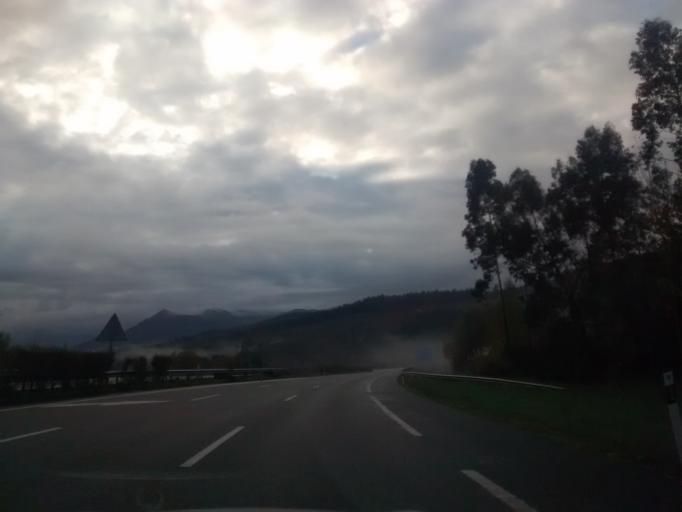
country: ES
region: Cantabria
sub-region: Provincia de Cantabria
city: Barcena de Cicero
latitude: 43.4072
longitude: -3.4967
